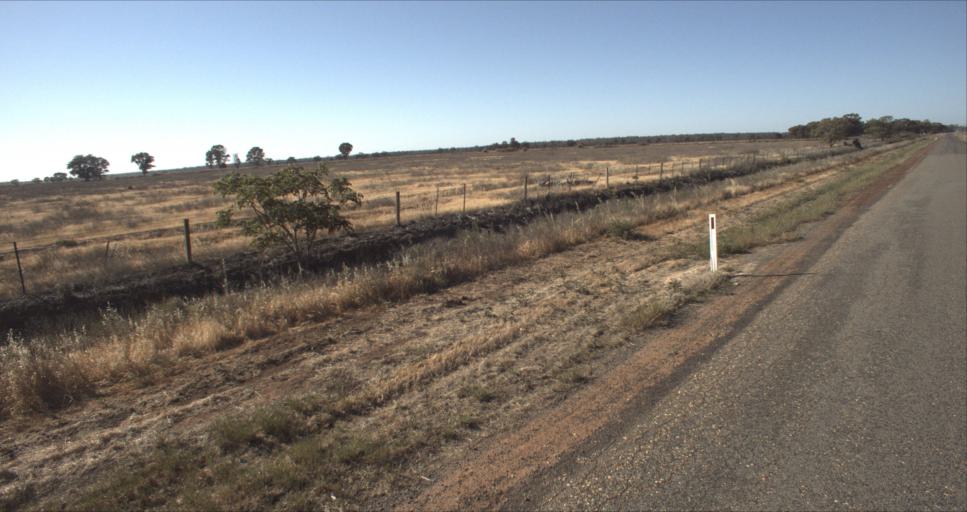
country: AU
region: New South Wales
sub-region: Leeton
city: Leeton
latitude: -34.5843
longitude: 146.2610
